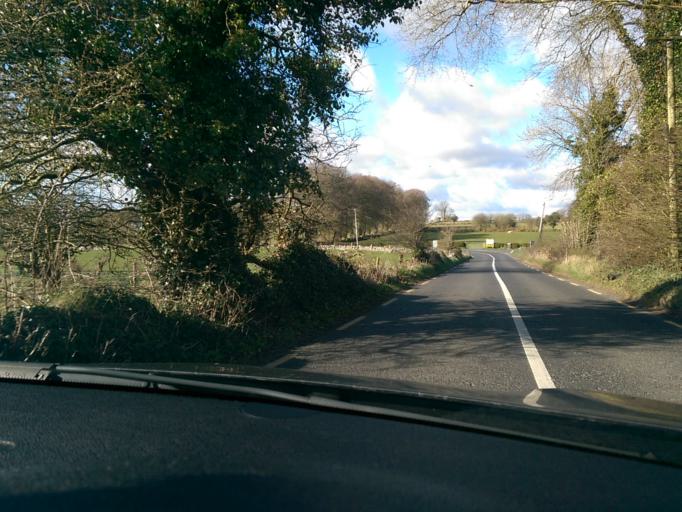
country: IE
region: Connaught
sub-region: Roscommon
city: Castlerea
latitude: 53.5436
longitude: -8.5520
